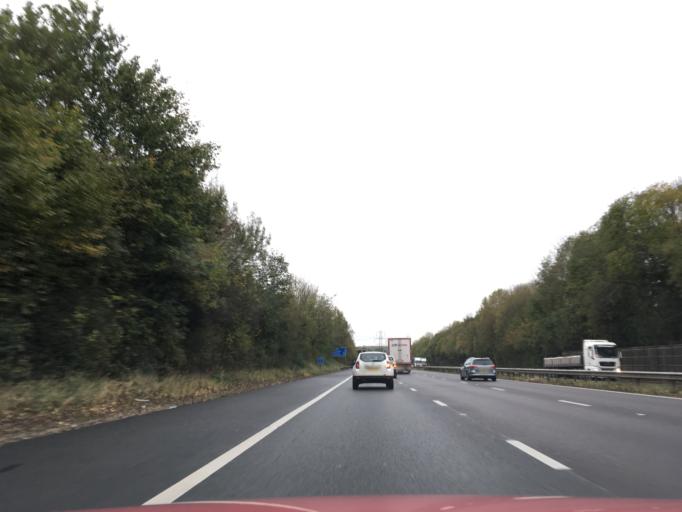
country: GB
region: England
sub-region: Hampshire
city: Eastleigh
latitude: 50.9894
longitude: -1.3614
